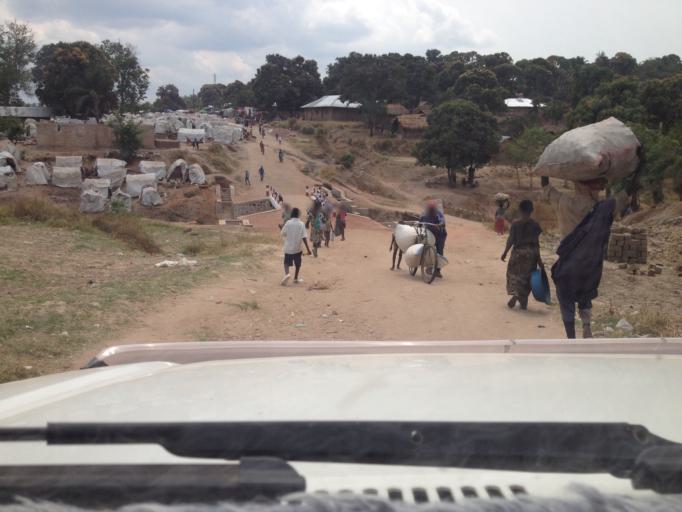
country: CD
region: Katanga
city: Kalemie
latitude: -5.9192
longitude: 29.1782
